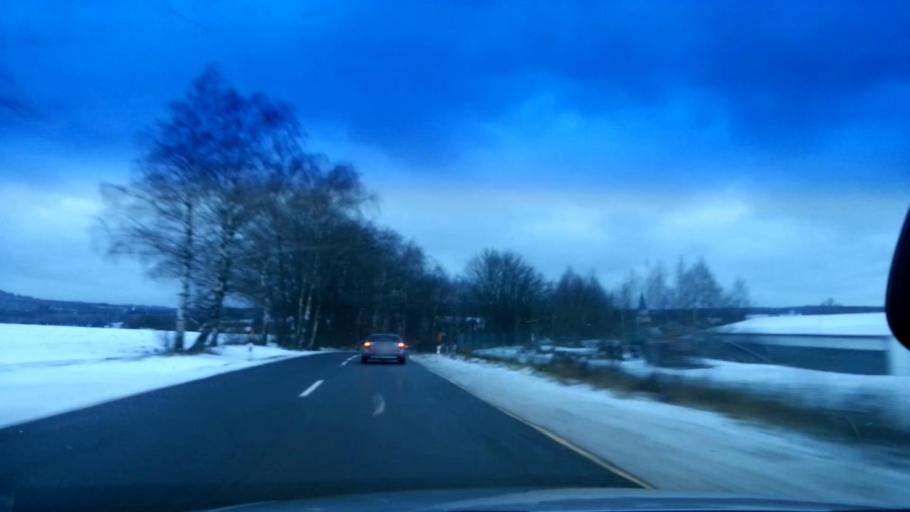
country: DE
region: Bavaria
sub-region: Upper Franconia
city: Kirchenlamitz
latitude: 50.1483
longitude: 11.9570
